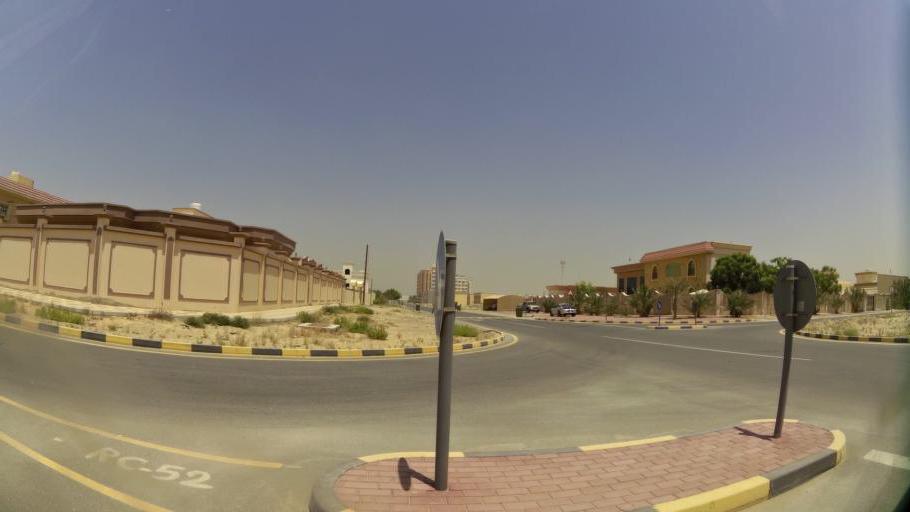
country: AE
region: Ajman
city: Ajman
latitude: 25.4077
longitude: 55.5200
